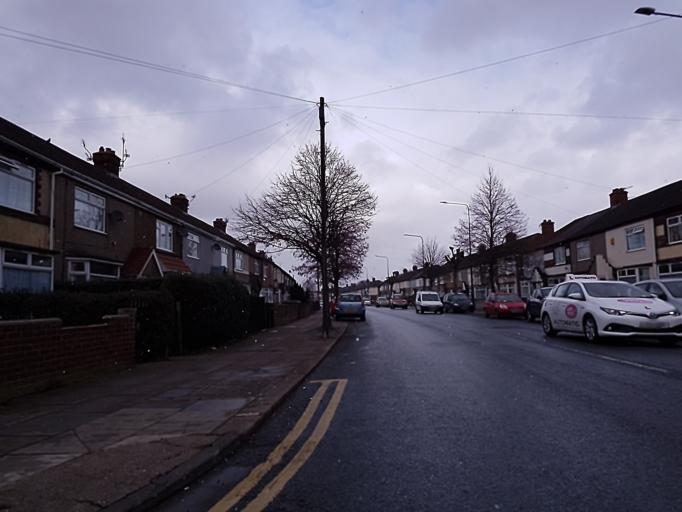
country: GB
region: England
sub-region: North East Lincolnshire
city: Grimbsy
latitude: 53.5689
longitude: -0.1002
